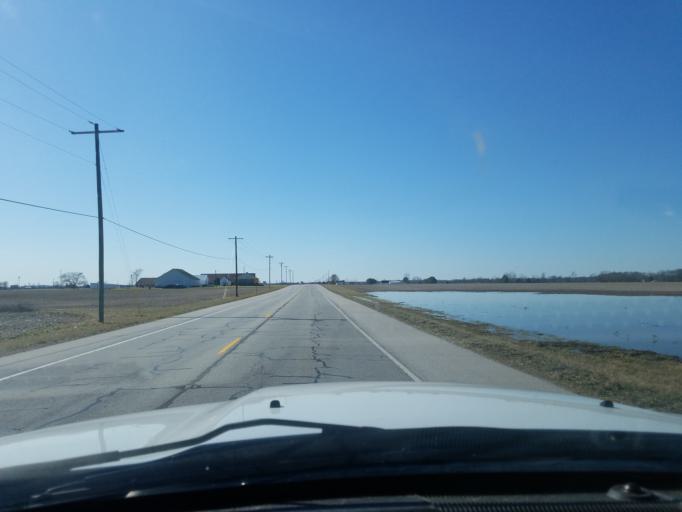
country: US
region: Indiana
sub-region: Shelby County
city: Shelbyville
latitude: 39.5045
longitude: -85.8101
